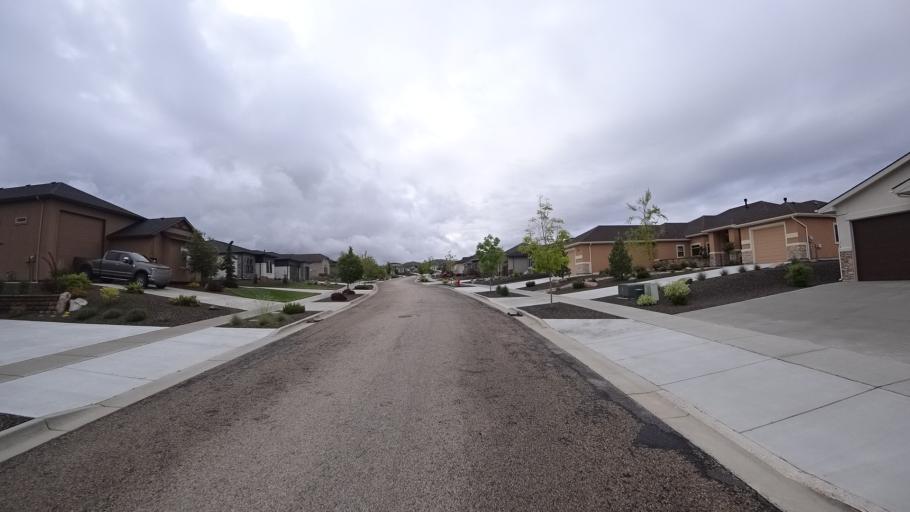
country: US
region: Idaho
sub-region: Ada County
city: Eagle
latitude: 43.7716
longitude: -116.2559
